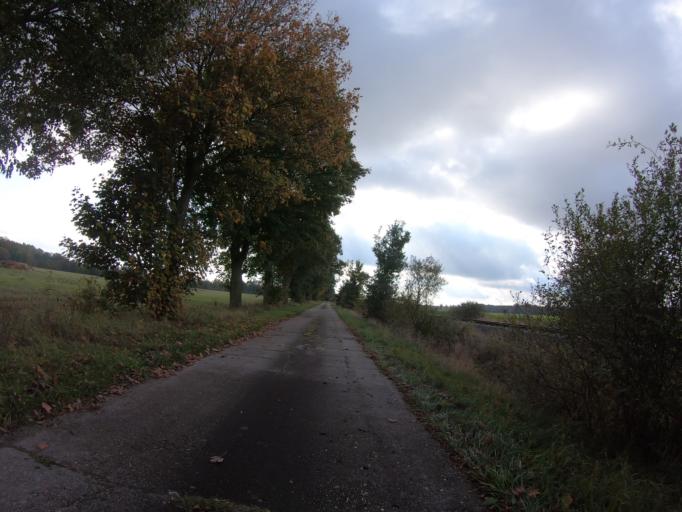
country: DE
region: Lower Saxony
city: Wahrenholz
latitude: 52.5822
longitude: 10.6102
